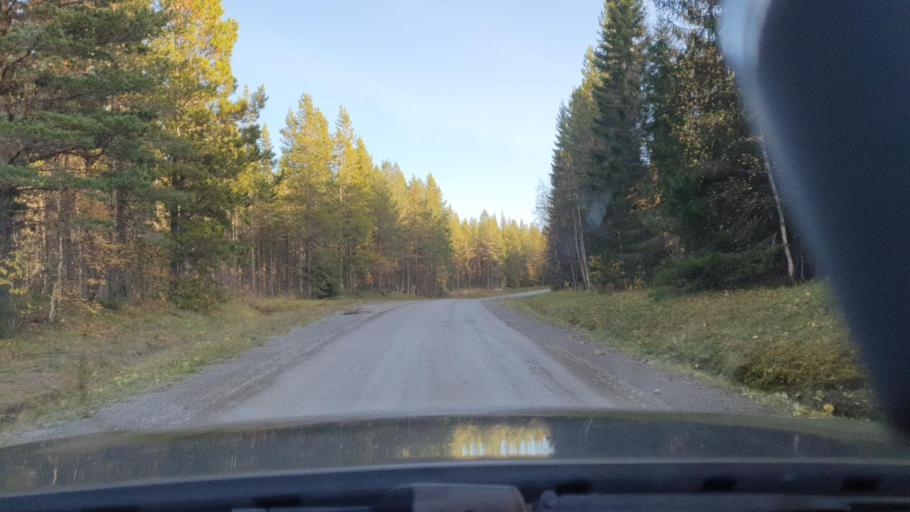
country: SE
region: Jaemtland
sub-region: Stroemsunds Kommun
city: Stroemsund
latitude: 63.5361
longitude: 15.6061
